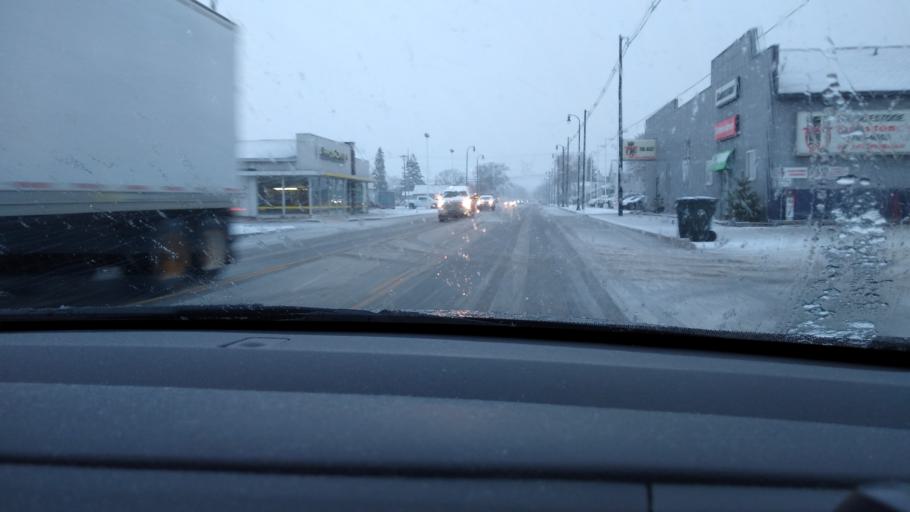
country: US
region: Michigan
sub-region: Delta County
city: Escanaba
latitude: 45.7510
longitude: -87.0718
